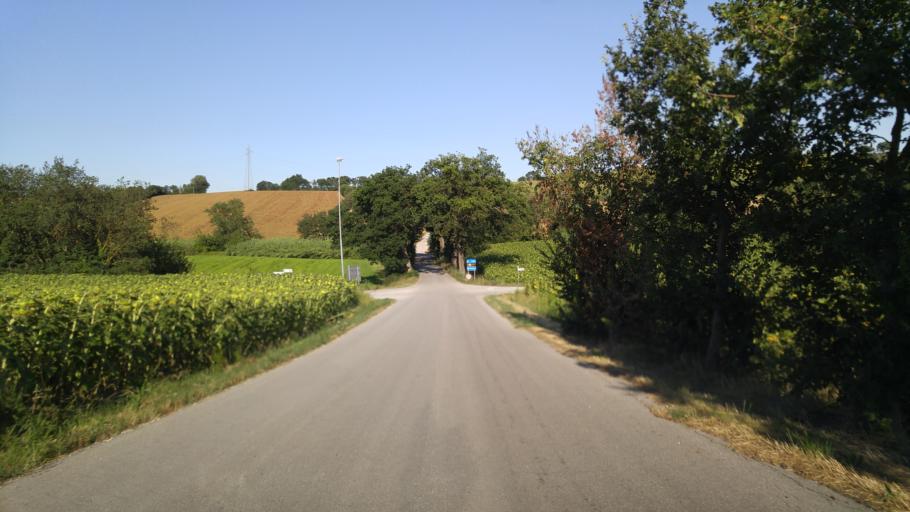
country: IT
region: The Marches
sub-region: Provincia di Pesaro e Urbino
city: Mombaroccio
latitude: 43.8114
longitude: 12.8798
